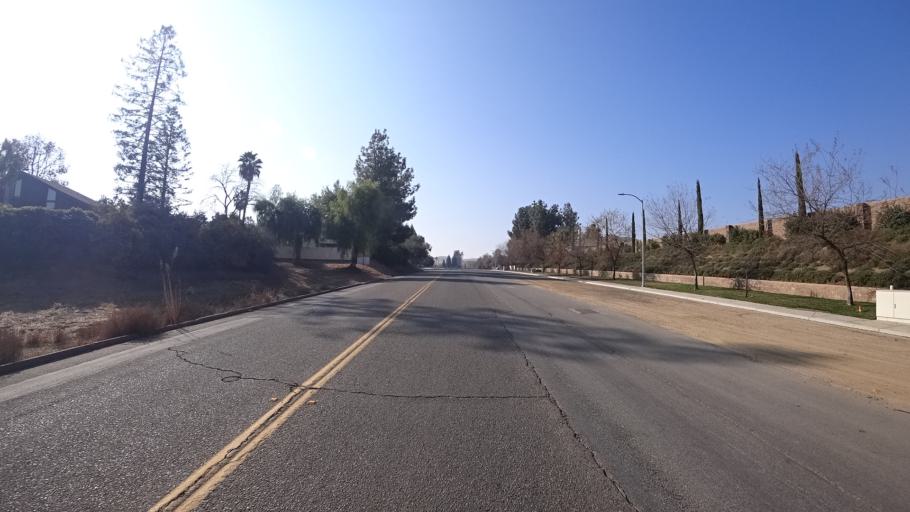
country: US
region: California
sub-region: Kern County
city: Oildale
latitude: 35.4324
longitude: -118.8668
